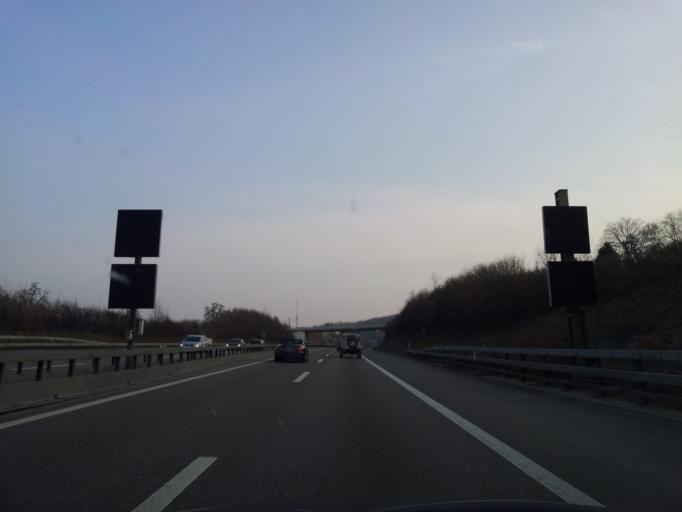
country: CH
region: Zurich
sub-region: Bezirk Dietikon
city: Urdorf / Oberurdorf
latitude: 47.3779
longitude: 8.4178
